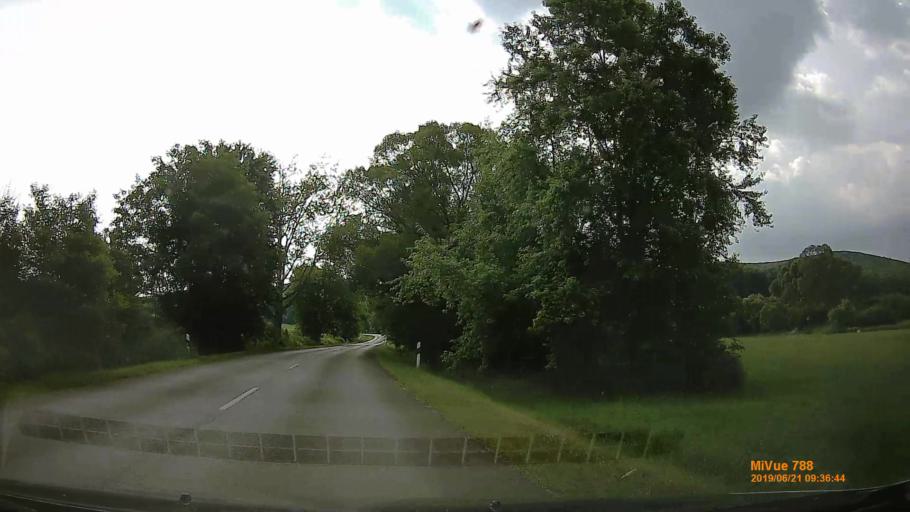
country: HU
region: Somogy
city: Taszar
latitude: 46.3159
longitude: 17.9067
